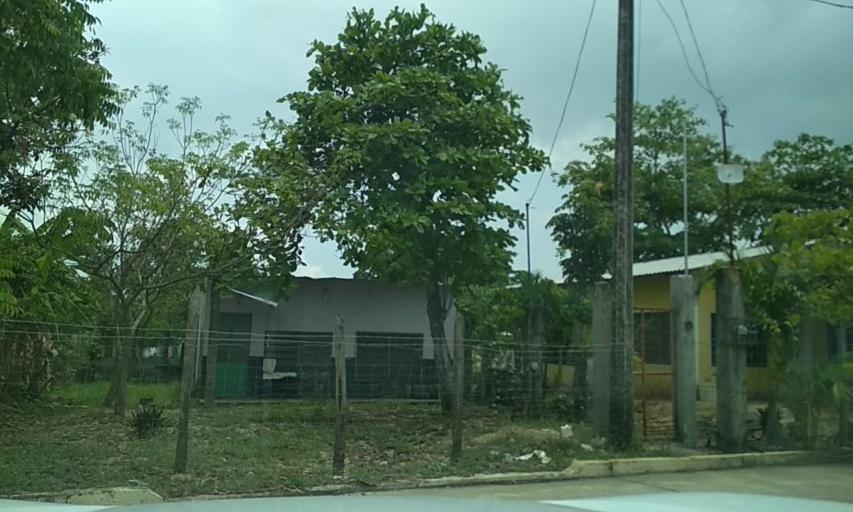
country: MX
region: Veracruz
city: Las Choapas
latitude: 17.8931
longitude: -94.0970
